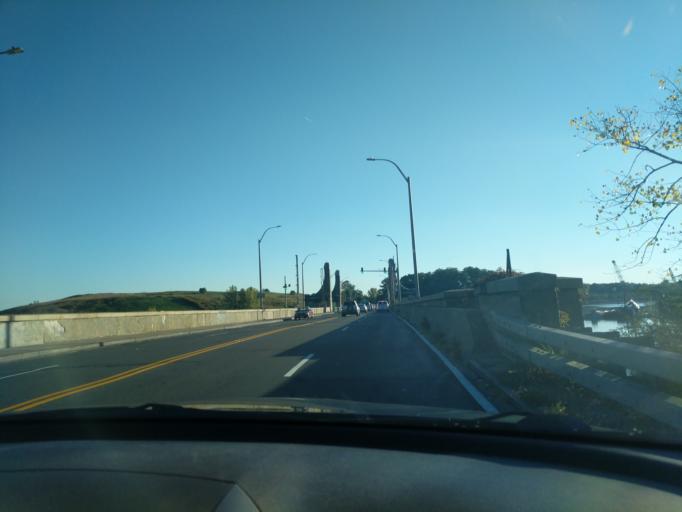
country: US
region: New York
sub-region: Bronx
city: Eastchester
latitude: 40.8633
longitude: -73.8150
